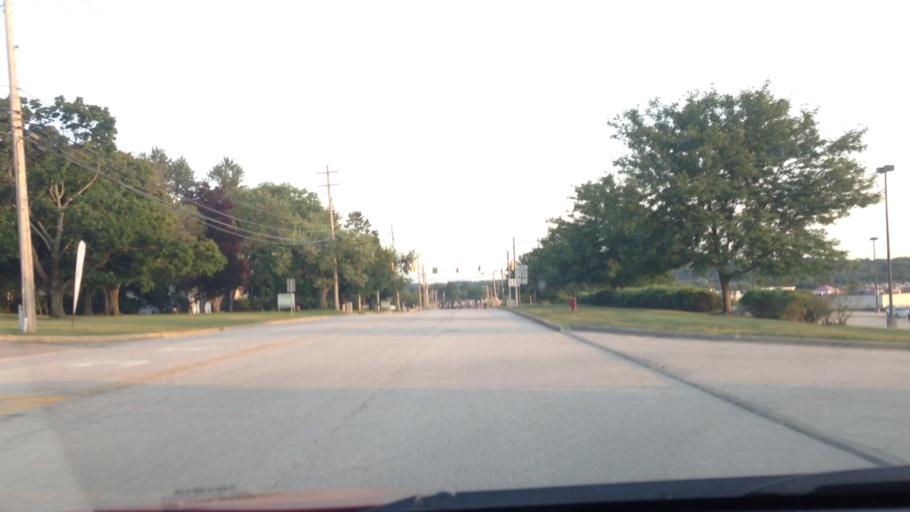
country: US
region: Ohio
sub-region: Summit County
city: Montrose-Ghent
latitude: 41.1408
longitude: -81.6374
